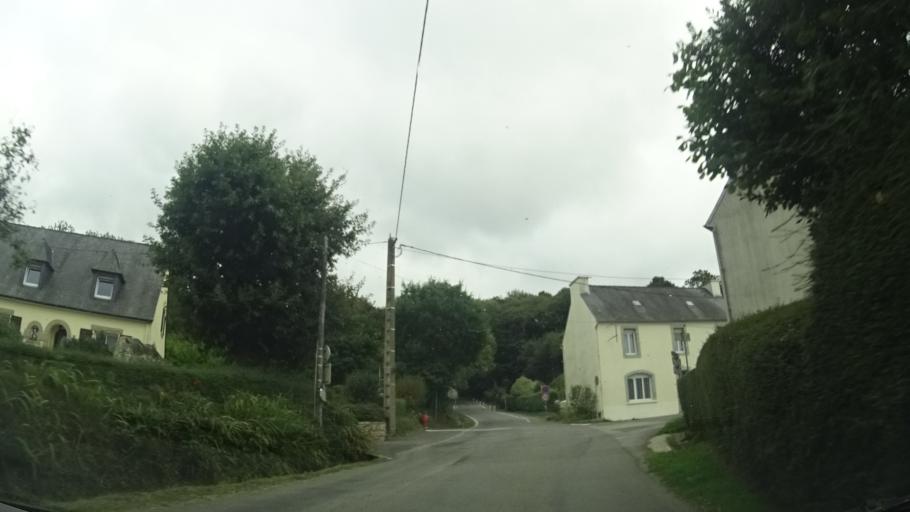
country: FR
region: Brittany
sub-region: Departement du Finistere
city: Le Relecq-Kerhuon
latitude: 48.3892
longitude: -4.3793
